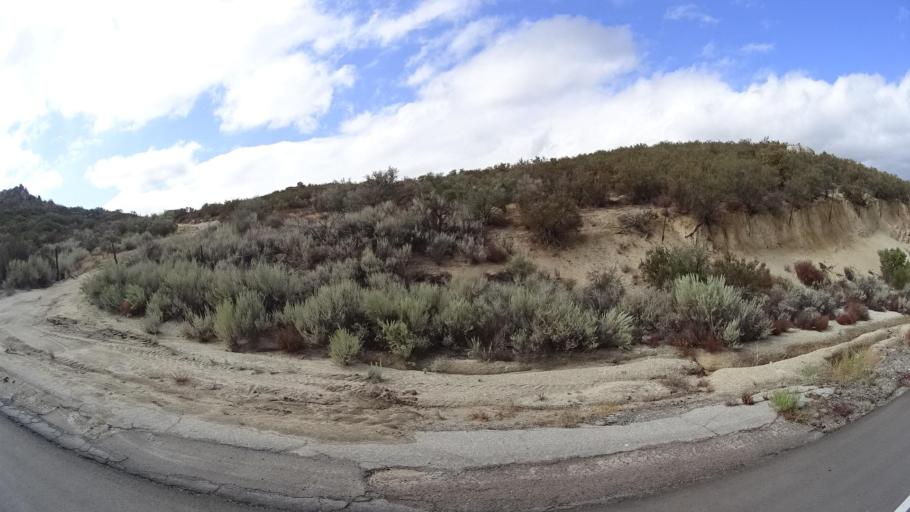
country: US
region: California
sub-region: San Diego County
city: Campo
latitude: 32.7221
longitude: -116.4103
